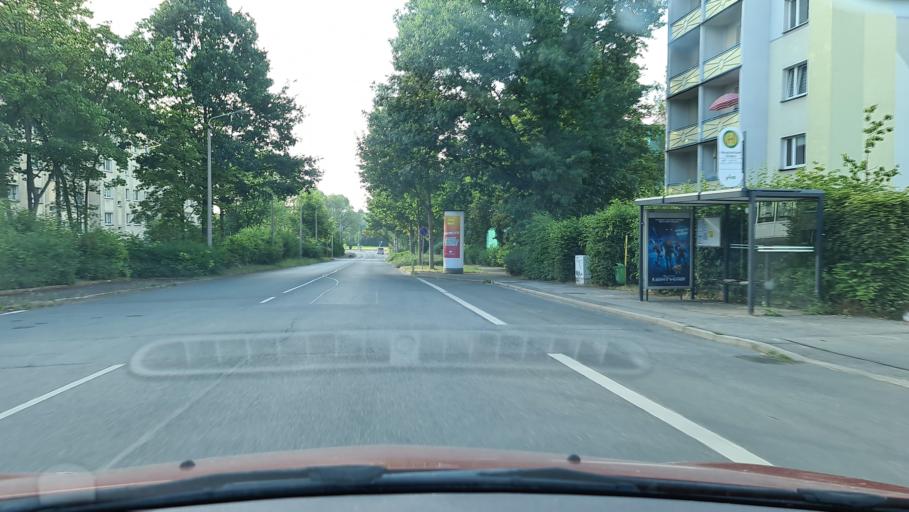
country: DE
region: Saxony
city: Lichtentanne
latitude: 50.6966
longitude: 12.4597
